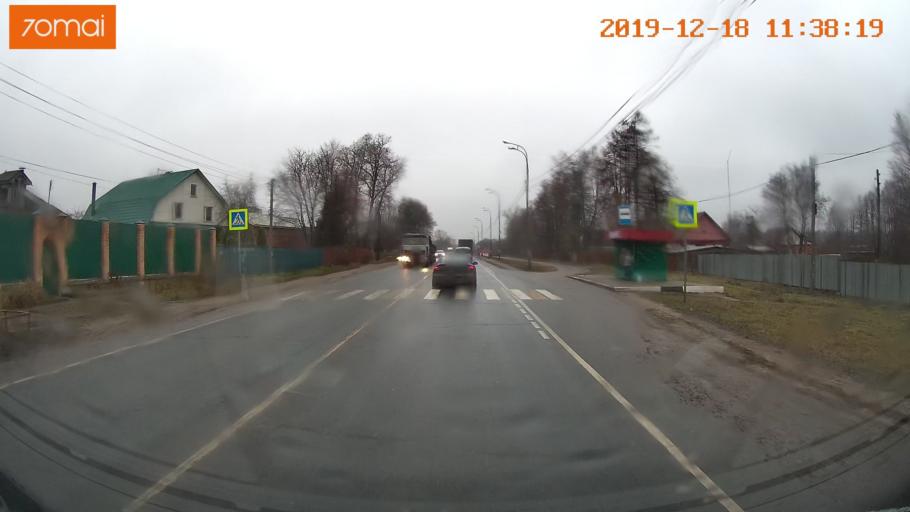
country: RU
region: Moskovskaya
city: Zvenigorod
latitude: 55.6959
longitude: 36.8886
